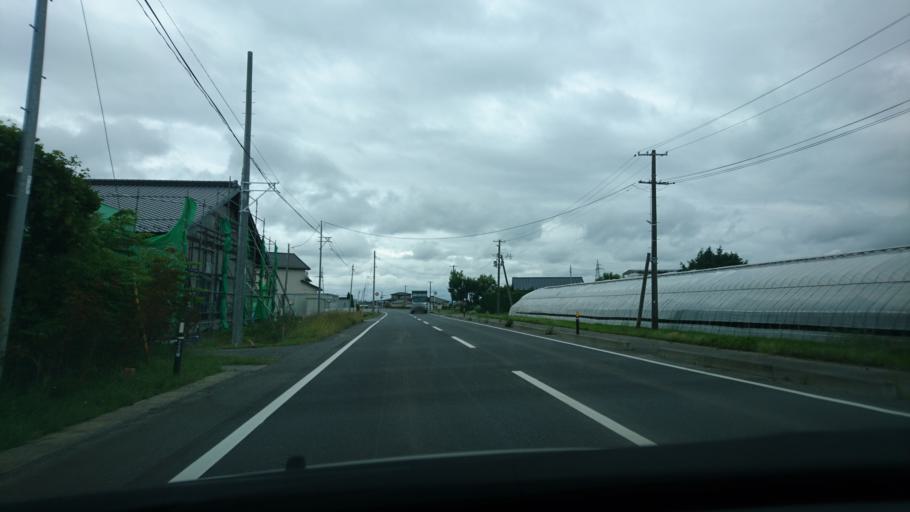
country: JP
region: Miyagi
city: Wakuya
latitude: 38.7146
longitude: 141.2584
